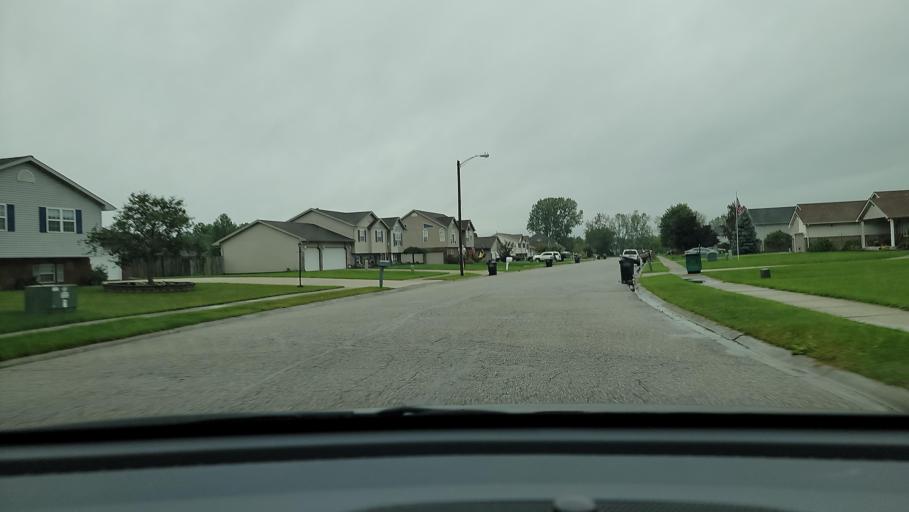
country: US
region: Indiana
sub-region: Porter County
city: Portage
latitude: 41.5628
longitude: -87.1678
